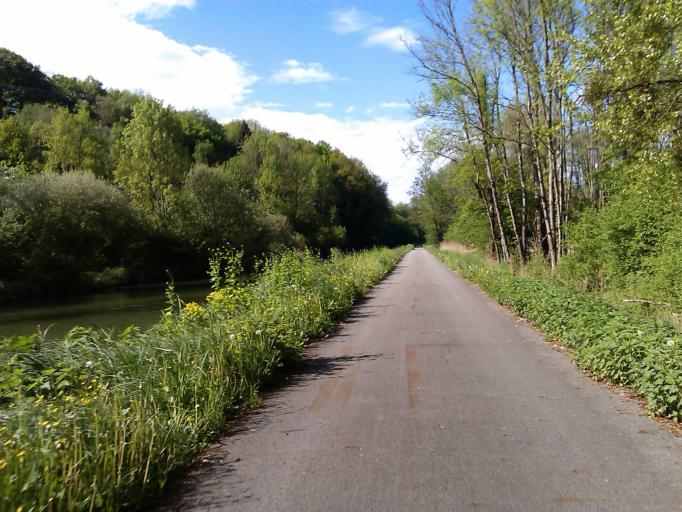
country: FR
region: Franche-Comte
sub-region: Departement du Doubs
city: Montenois
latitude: 47.4394
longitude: 6.5980
